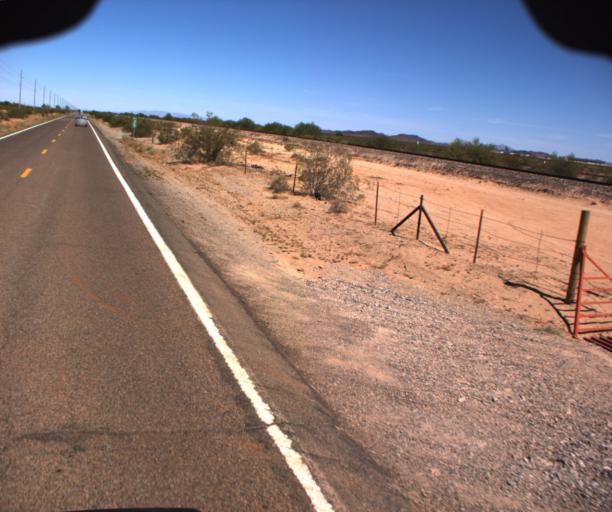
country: US
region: Arizona
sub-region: La Paz County
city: Salome
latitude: 33.8525
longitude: -113.9064
